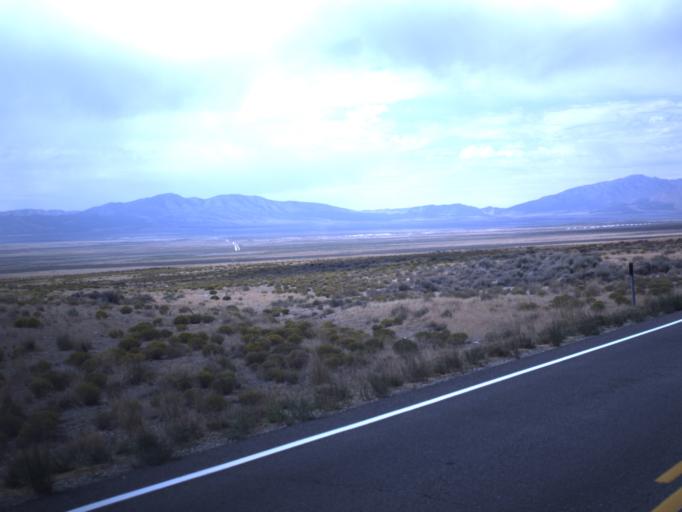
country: US
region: Utah
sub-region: Utah County
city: Eagle Mountain
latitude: 40.2611
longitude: -112.2319
